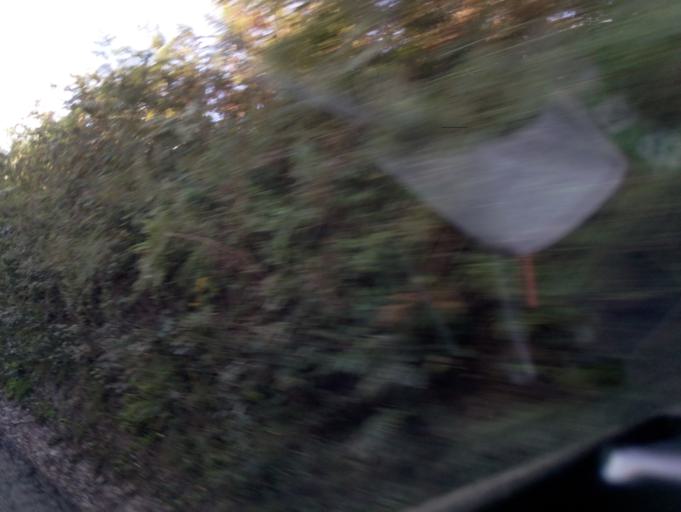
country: GB
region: England
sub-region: Devon
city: Dartmouth
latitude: 50.3414
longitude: -3.6081
